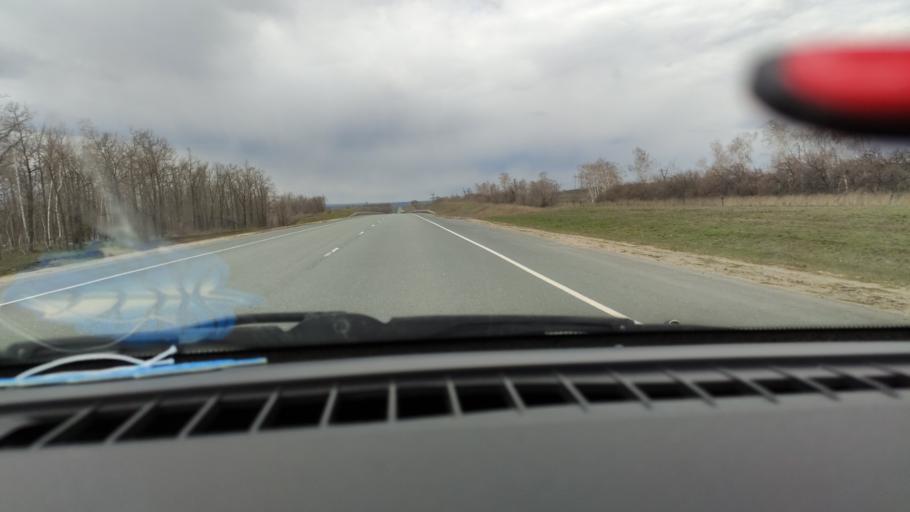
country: RU
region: Saratov
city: Yelshanka
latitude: 51.8219
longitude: 46.3290
